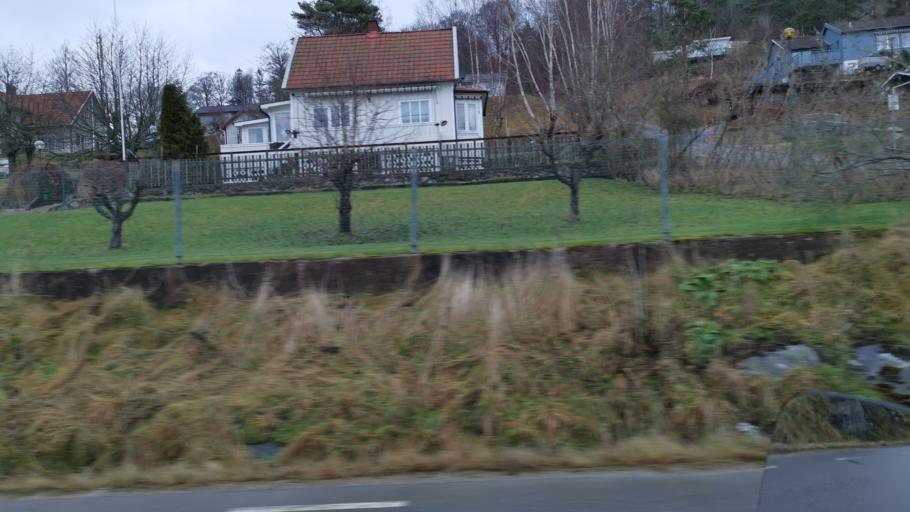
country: SE
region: Vaestra Goetaland
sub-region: Orust
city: Henan
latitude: 58.3394
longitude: 11.7089
